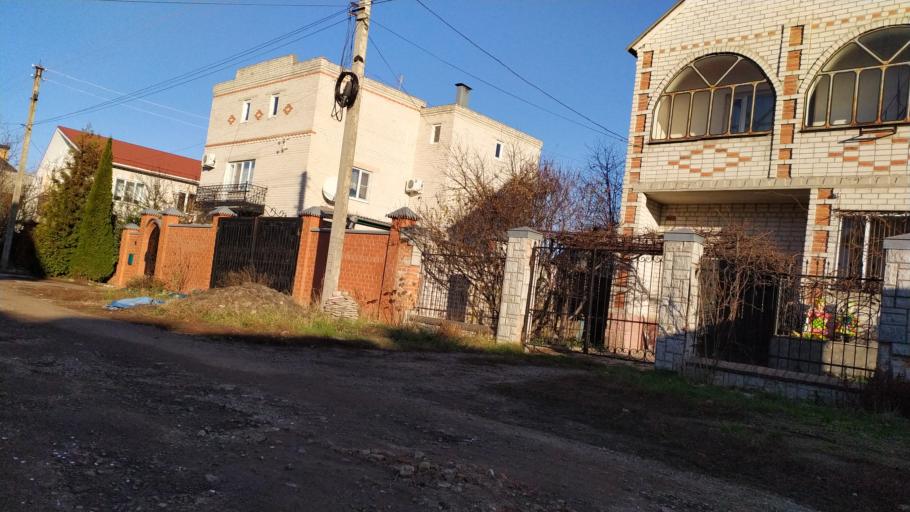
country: RU
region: Kursk
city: Kursk
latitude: 51.6453
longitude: 36.1378
